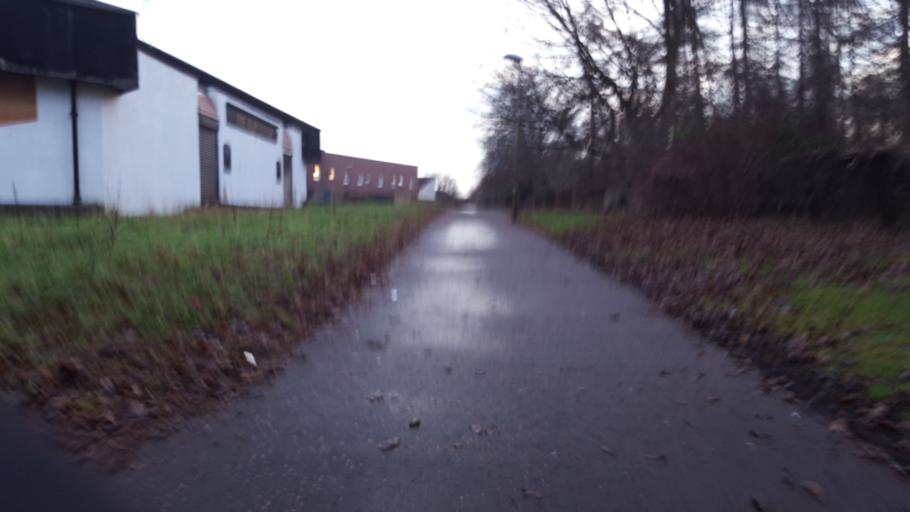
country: GB
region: Scotland
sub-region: West Lothian
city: Livingston
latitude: 55.9074
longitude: -3.5232
